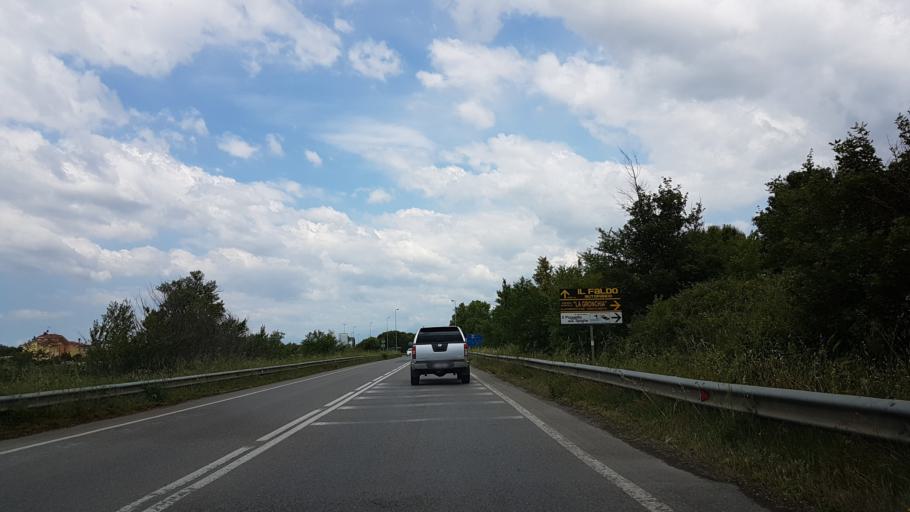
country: IT
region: Tuscany
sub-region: Provincia di Livorno
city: Vicarello
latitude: 43.6073
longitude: 10.4740
